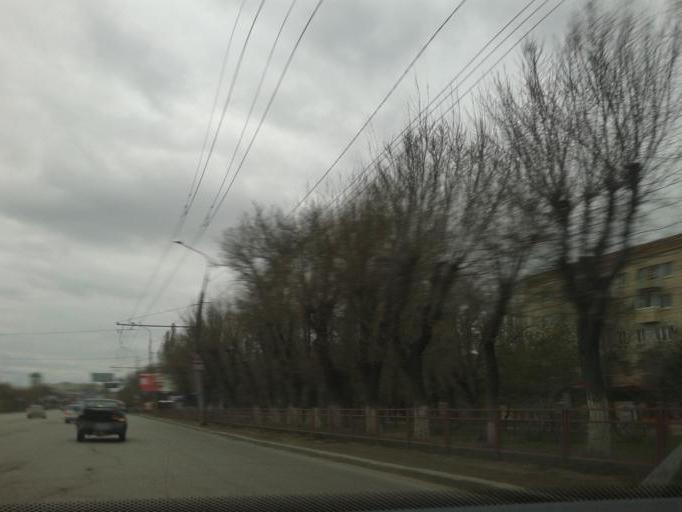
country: RU
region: Volgograd
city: Volgograd
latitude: 48.7462
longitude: 44.4876
